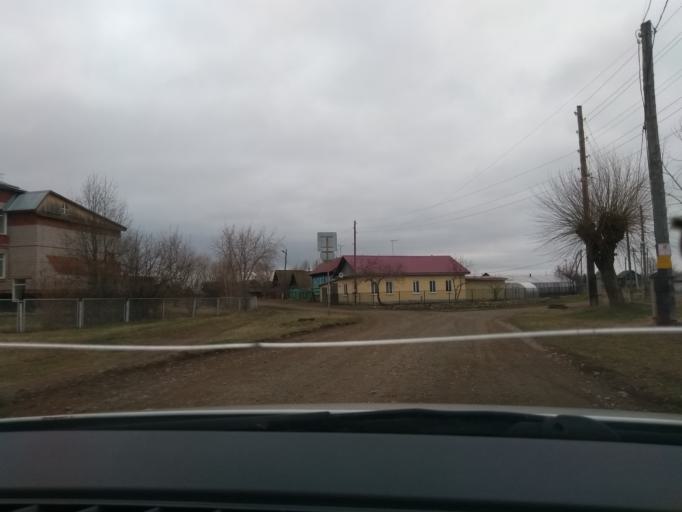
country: RU
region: Perm
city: Orda
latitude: 57.2154
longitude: 56.5920
